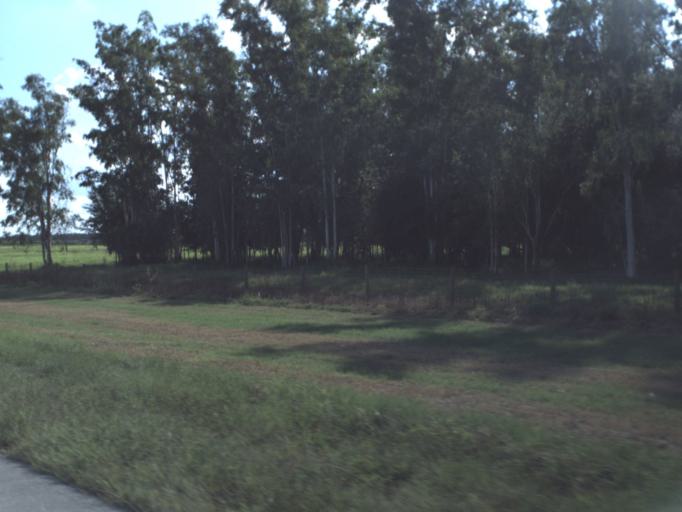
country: US
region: Florida
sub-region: Polk County
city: Mulberry
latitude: 27.7477
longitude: -81.9963
